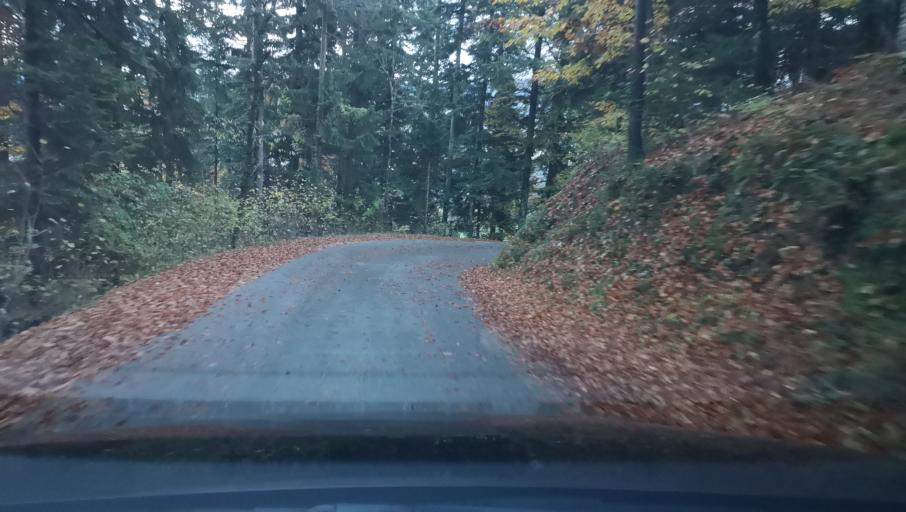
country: AT
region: Styria
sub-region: Politischer Bezirk Weiz
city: Birkfeld
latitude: 47.3336
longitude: 15.6742
